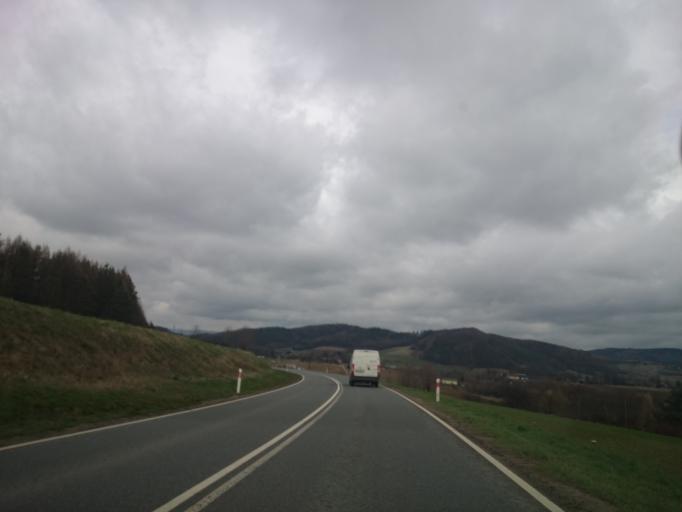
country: PL
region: Lower Silesian Voivodeship
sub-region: Powiat klodzki
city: Bystrzyca Klodzka
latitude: 50.3573
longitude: 16.6717
